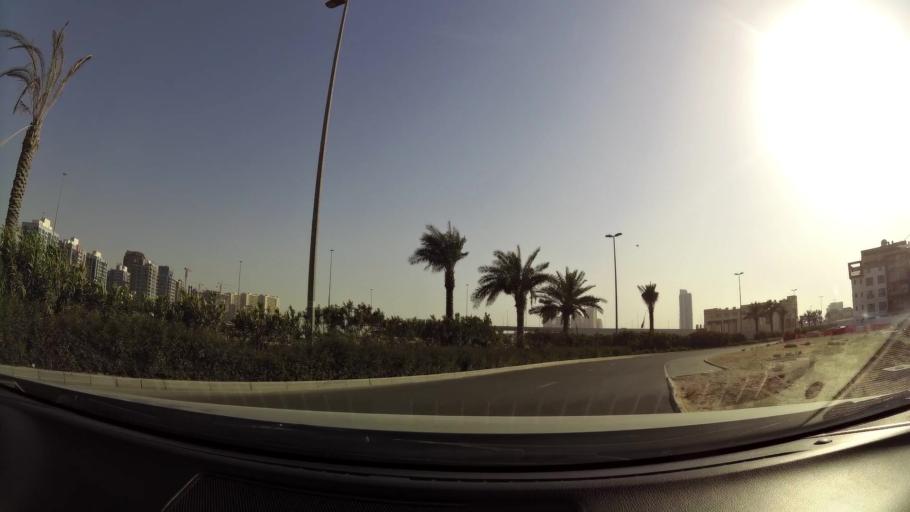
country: AE
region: Dubai
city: Dubai
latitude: 25.0459
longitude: 55.2050
